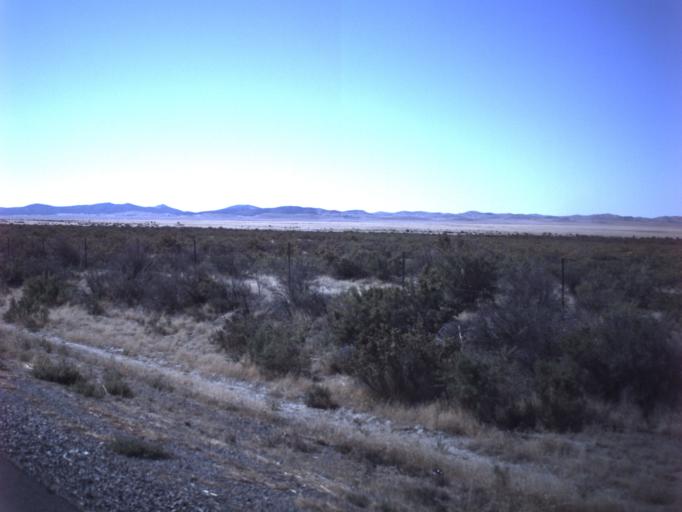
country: US
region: Utah
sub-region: Tooele County
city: Grantsville
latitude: 40.3516
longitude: -112.7454
